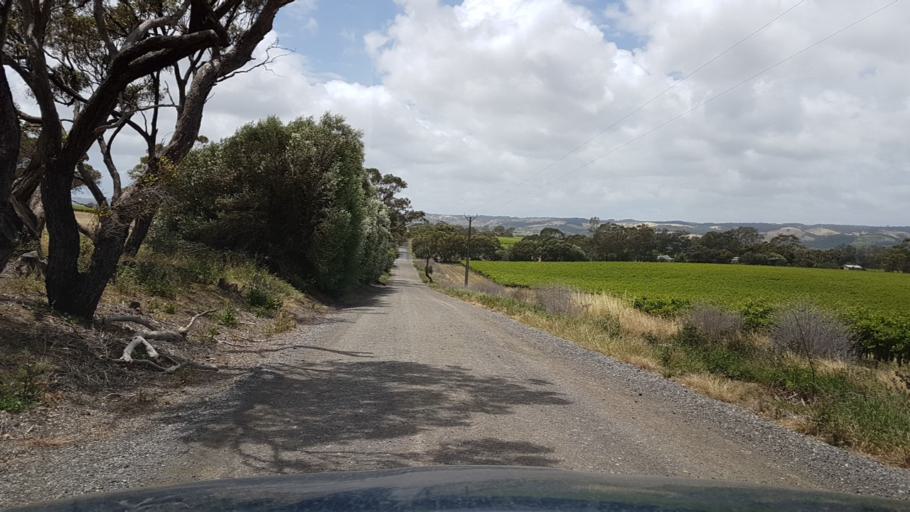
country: AU
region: South Australia
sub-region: Onkaparinga
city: McLaren Vale
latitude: -35.2409
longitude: 138.5359
